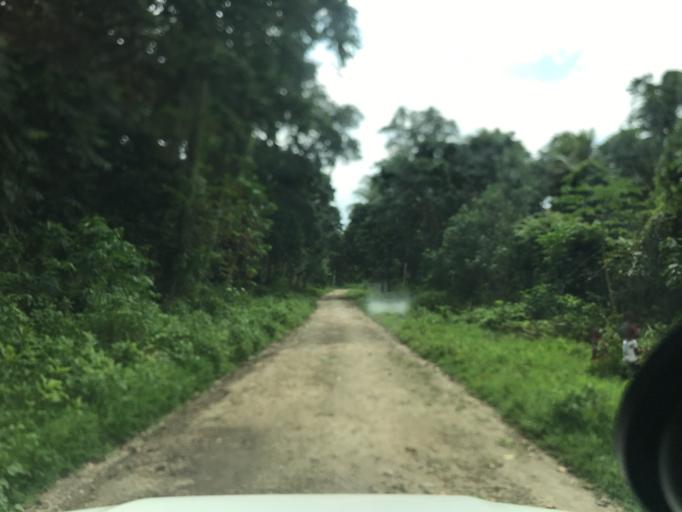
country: VU
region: Sanma
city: Port-Olry
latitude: -15.1678
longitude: 166.9487
